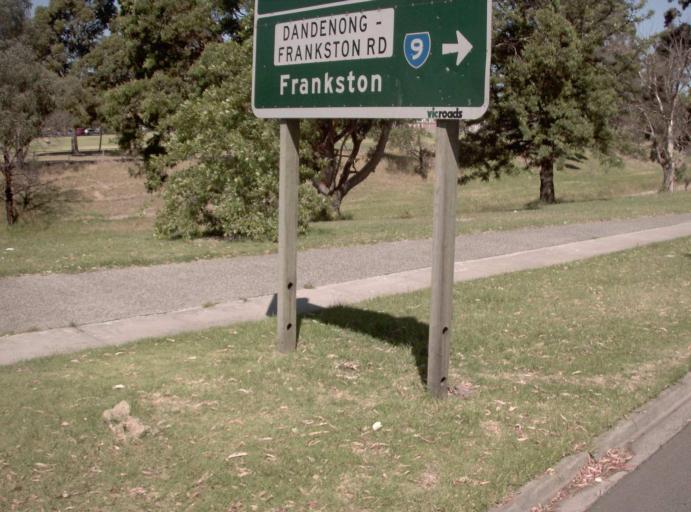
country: AU
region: Victoria
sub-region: Casey
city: Doveton
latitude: -37.9950
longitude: 145.2178
